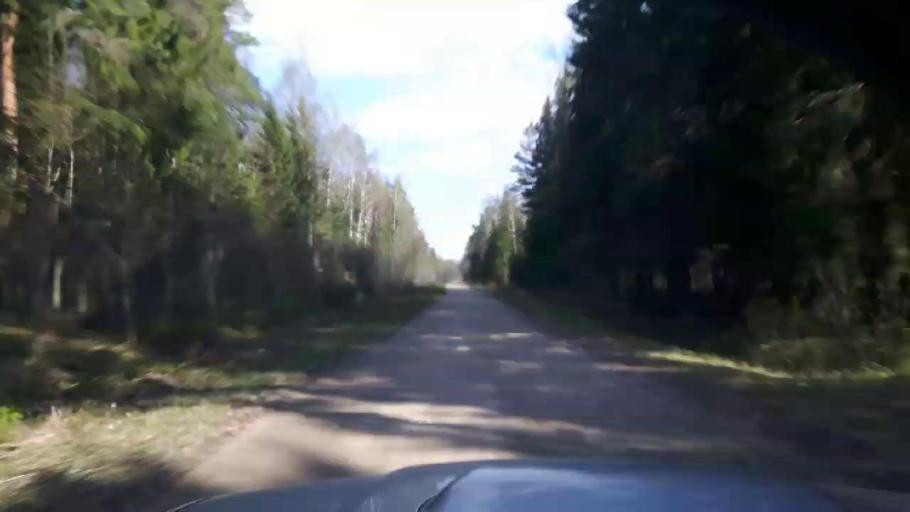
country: EE
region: Paernumaa
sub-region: Tootsi vald
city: Tootsi
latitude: 58.4455
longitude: 24.8707
